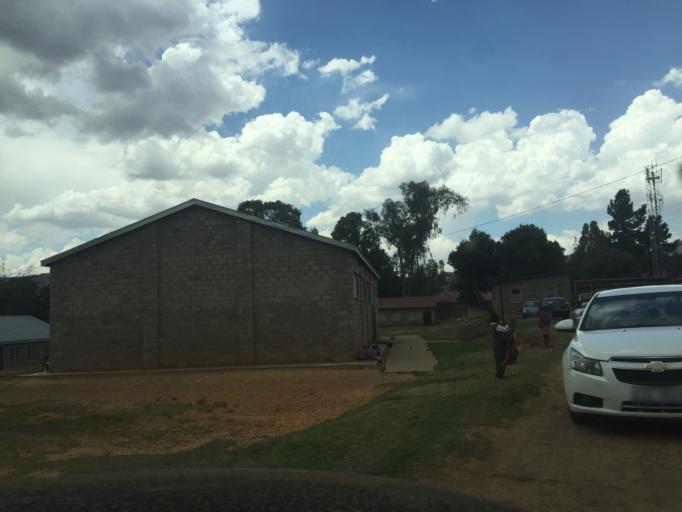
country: LS
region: Maseru
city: Nako
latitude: -29.4484
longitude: 27.7239
